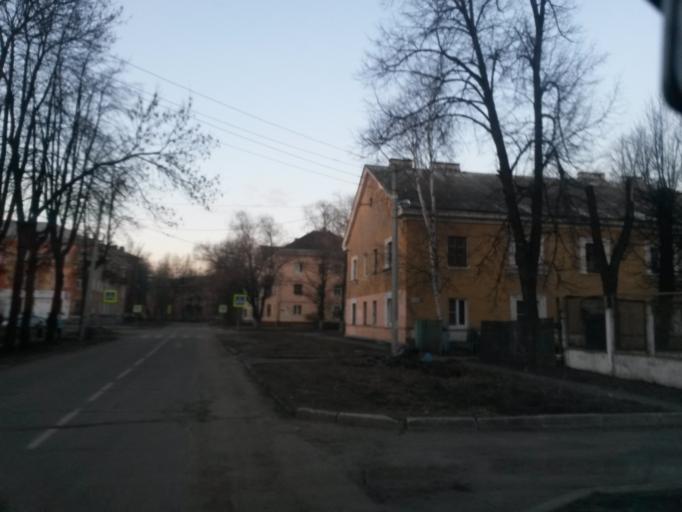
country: RU
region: Jaroslavl
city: Yaroslavl
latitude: 57.6344
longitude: 39.8409
